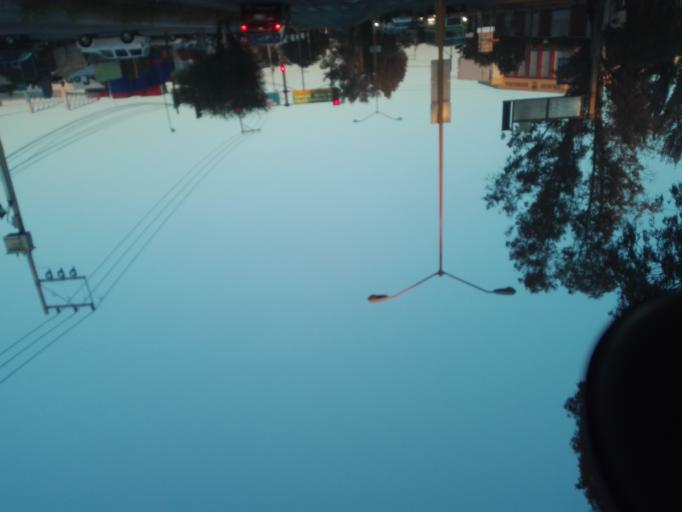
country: MX
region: Aguascalientes
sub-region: Aguascalientes
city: La Loma de los Negritos
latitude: 21.8678
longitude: -102.3283
